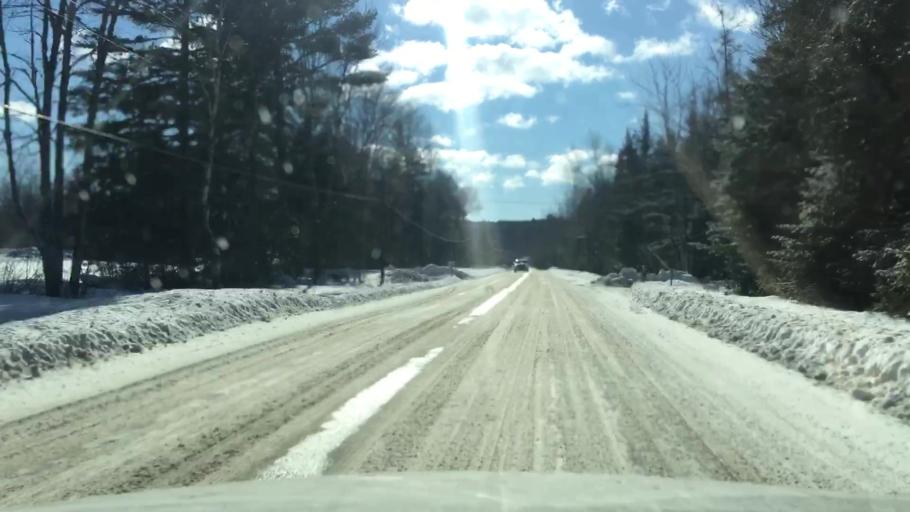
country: US
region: Maine
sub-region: Washington County
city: Calais
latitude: 45.0686
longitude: -67.4745
